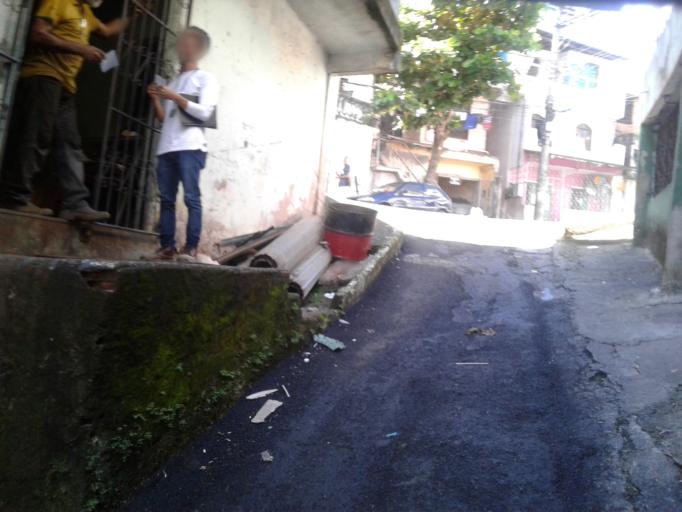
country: BR
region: Bahia
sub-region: Salvador
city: Salvador
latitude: -12.9124
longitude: -38.4687
